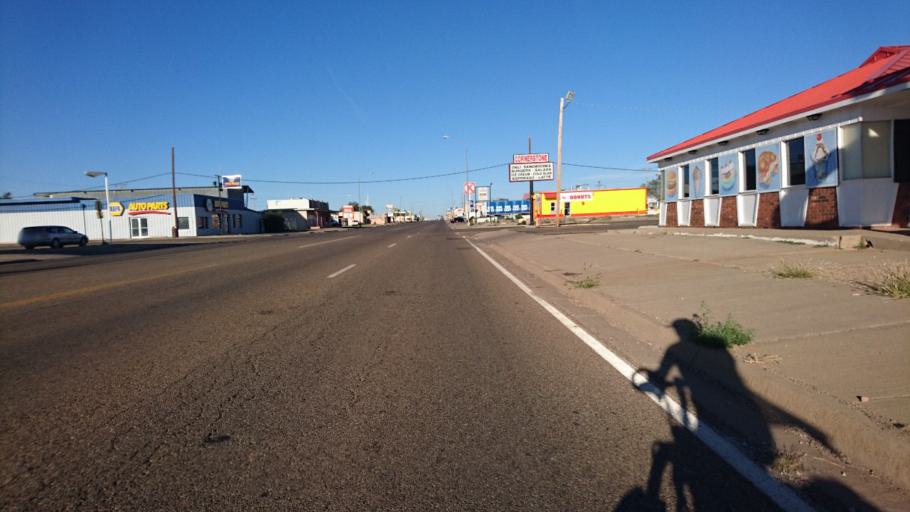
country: US
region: New Mexico
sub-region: Quay County
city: Tucumcari
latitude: 35.1719
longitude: -103.7180
